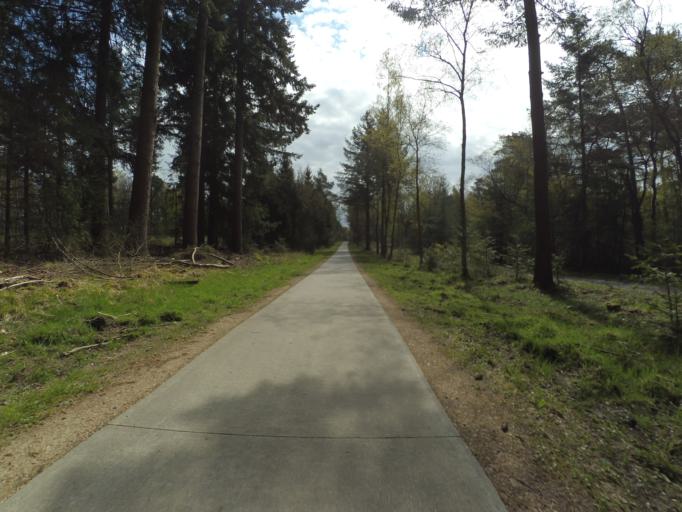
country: NL
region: Gelderland
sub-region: Gemeente Epe
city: Epe
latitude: 52.3805
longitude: 5.9310
